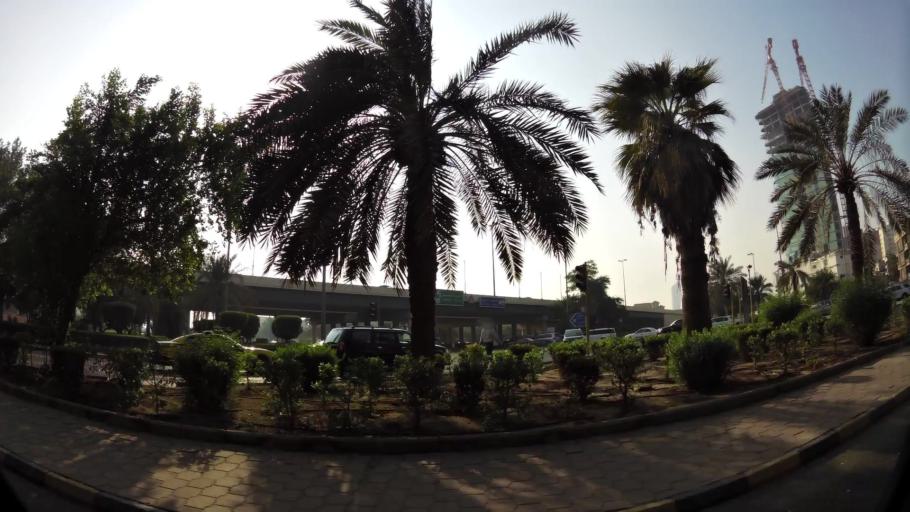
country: KW
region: Al Asimah
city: Ad Dasmah
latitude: 29.3661
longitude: 48.0115
